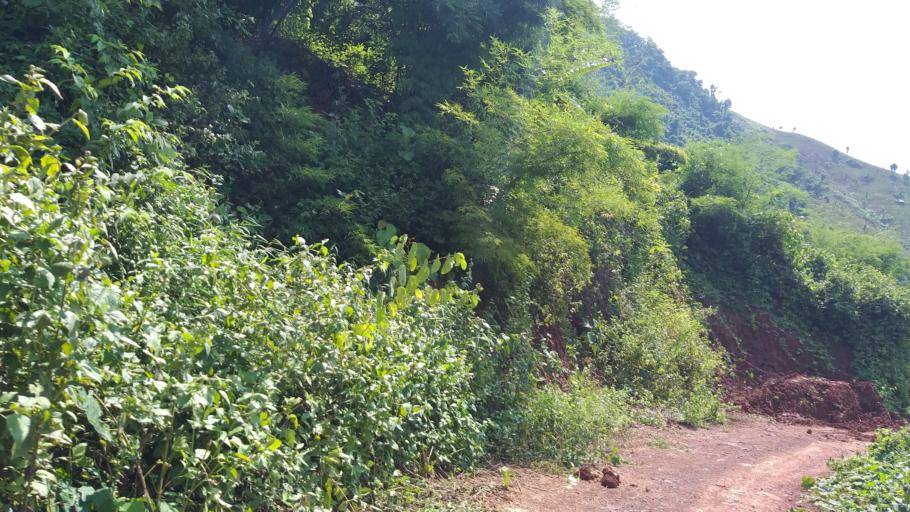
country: LA
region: Phongsali
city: Khoa
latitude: 21.2946
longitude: 102.5469
